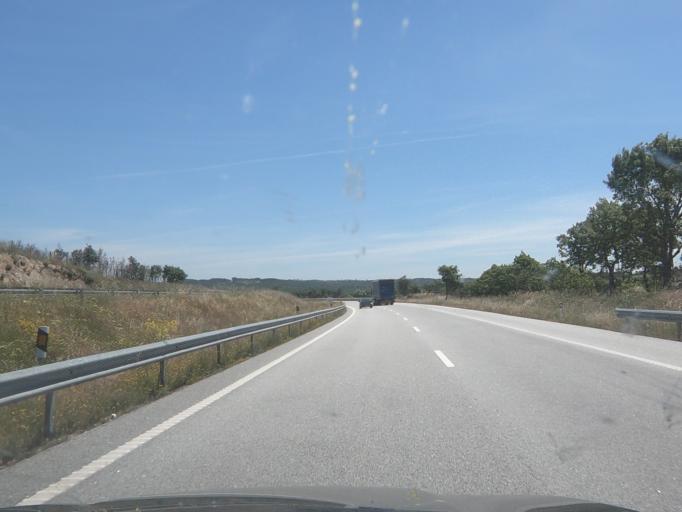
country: PT
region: Guarda
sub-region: Pinhel
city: Pinhel
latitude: 40.6033
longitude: -7.0489
